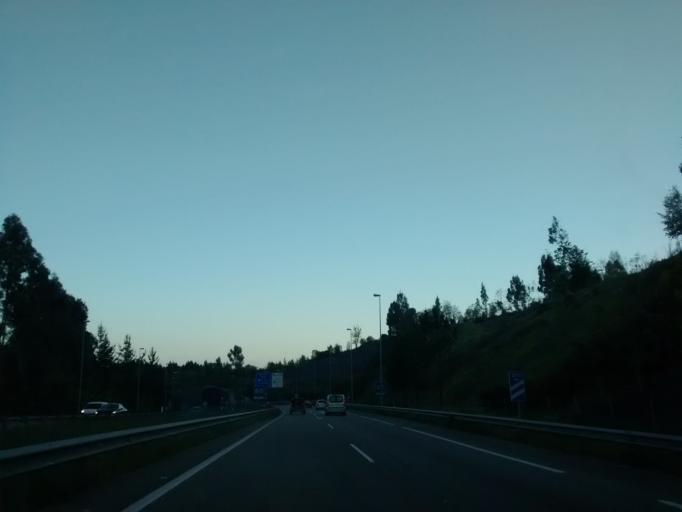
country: ES
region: Asturias
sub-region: Province of Asturias
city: Arriba
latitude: 43.5071
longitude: -5.5949
